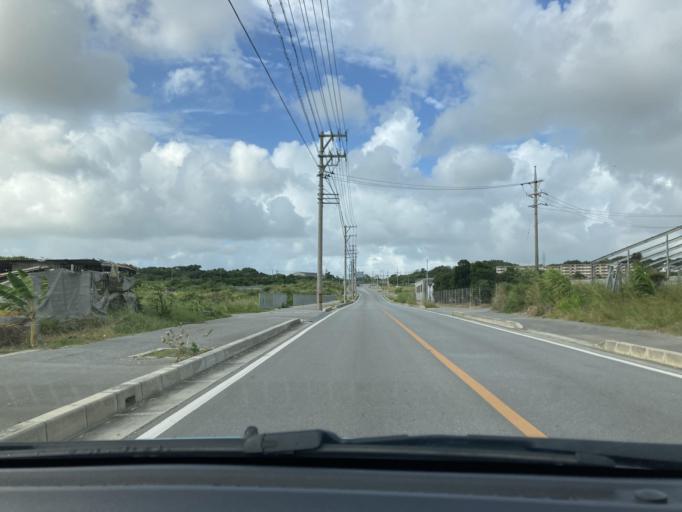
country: JP
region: Okinawa
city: Itoman
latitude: 26.1148
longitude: 127.6920
